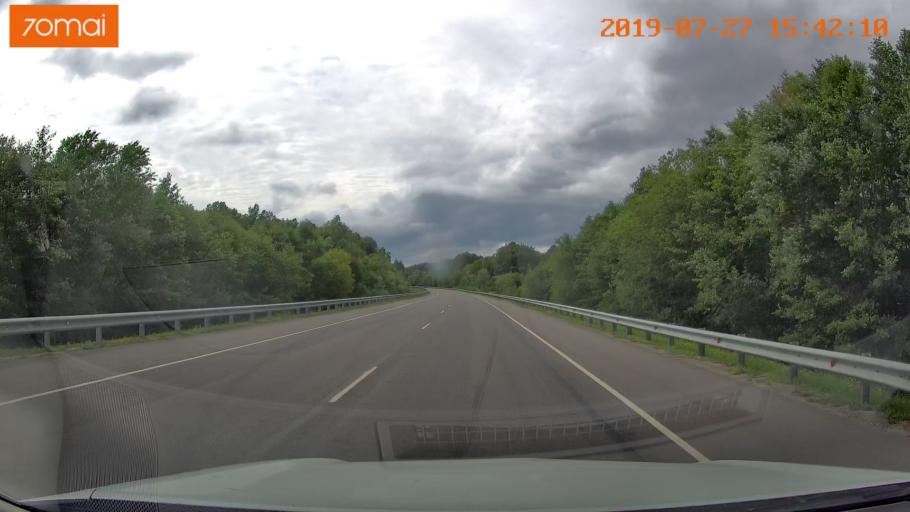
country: RU
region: Kaliningrad
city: Gusev
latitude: 54.6175
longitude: 22.2226
